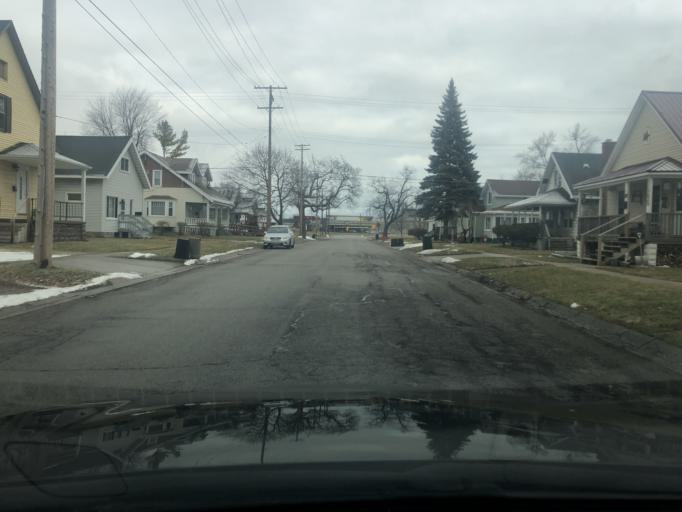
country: US
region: Michigan
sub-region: Saint Clair County
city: Port Huron
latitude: 42.9944
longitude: -82.4360
